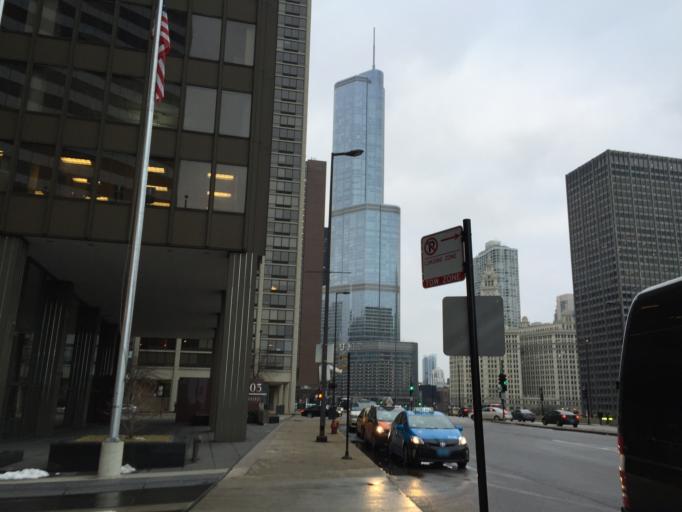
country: US
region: Illinois
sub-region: Cook County
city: Chicago
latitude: 41.8876
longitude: -87.6196
